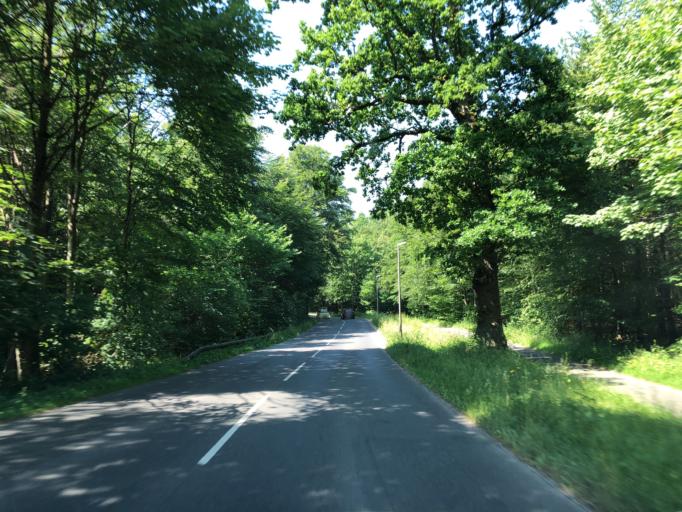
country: DK
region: South Denmark
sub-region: Kolding Kommune
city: Kolding
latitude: 55.5133
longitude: 9.4900
